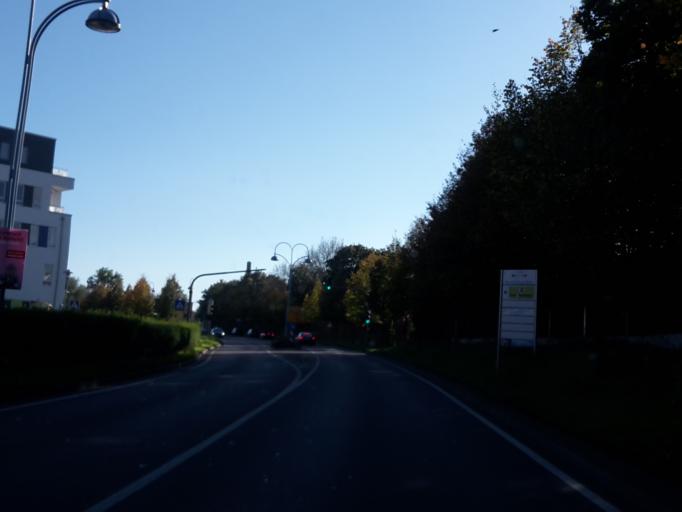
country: DE
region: Hesse
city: Viernheim
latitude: 49.5419
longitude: 8.5946
